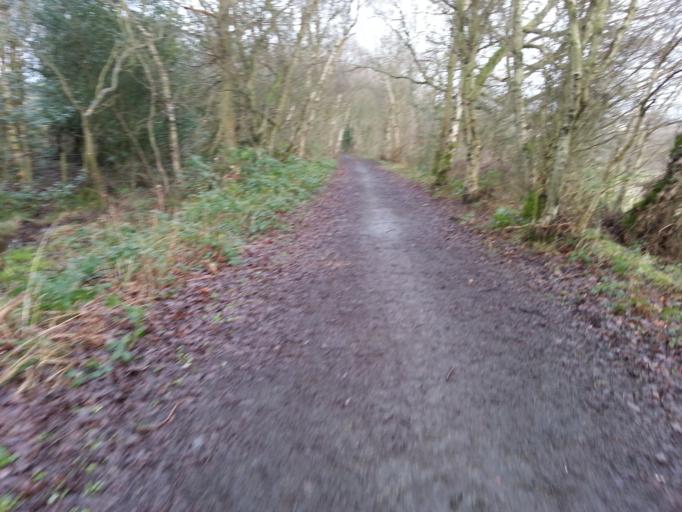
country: GB
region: England
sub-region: County Durham
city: Crook
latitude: 54.7543
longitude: -1.7317
